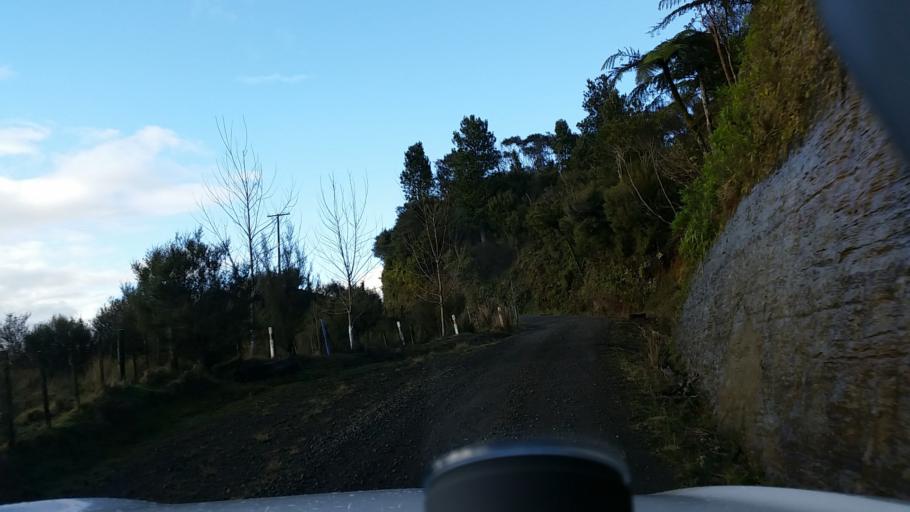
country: NZ
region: Taranaki
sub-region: South Taranaki District
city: Eltham
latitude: -39.4195
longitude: 174.5564
